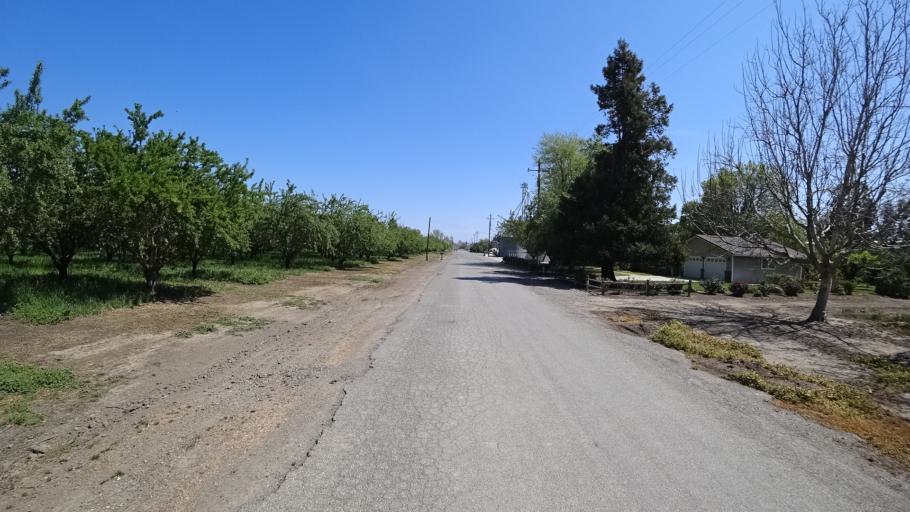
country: US
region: California
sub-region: Glenn County
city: Willows
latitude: 39.5363
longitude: -122.0215
